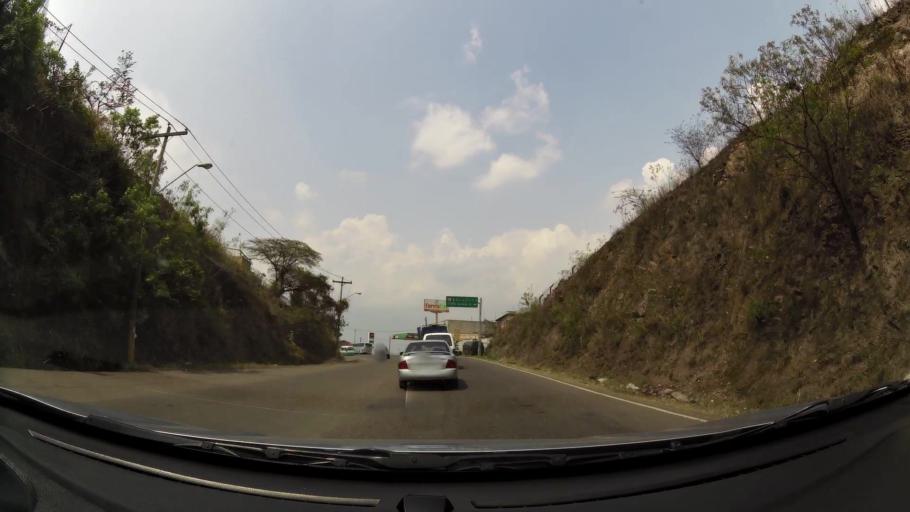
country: HN
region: Francisco Morazan
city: El Lolo
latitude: 14.1233
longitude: -87.2249
